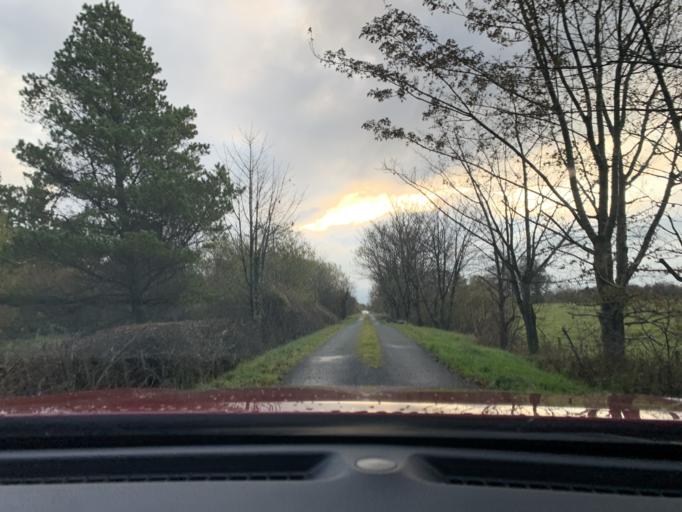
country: IE
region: Connaught
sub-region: Sligo
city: Ballymote
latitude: 54.0327
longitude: -8.5325
